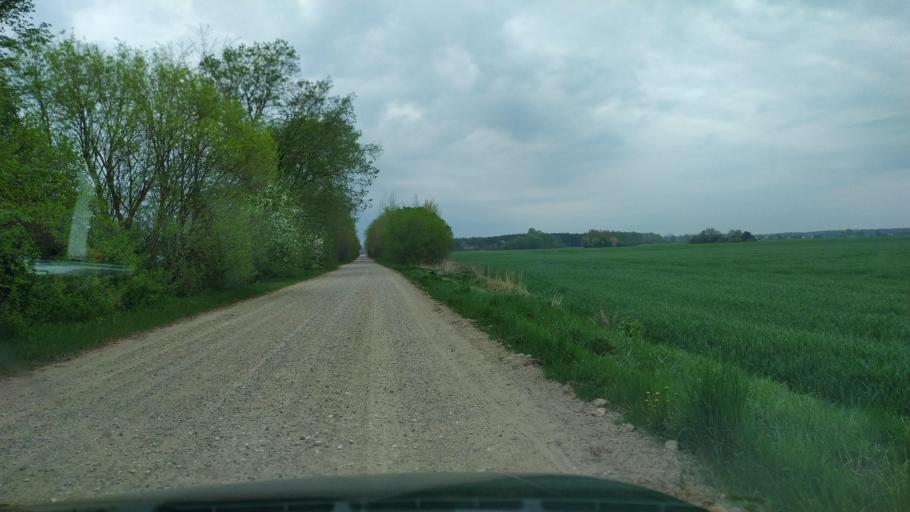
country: BY
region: Brest
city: Zhabinka
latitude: 52.1368
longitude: 24.0900
